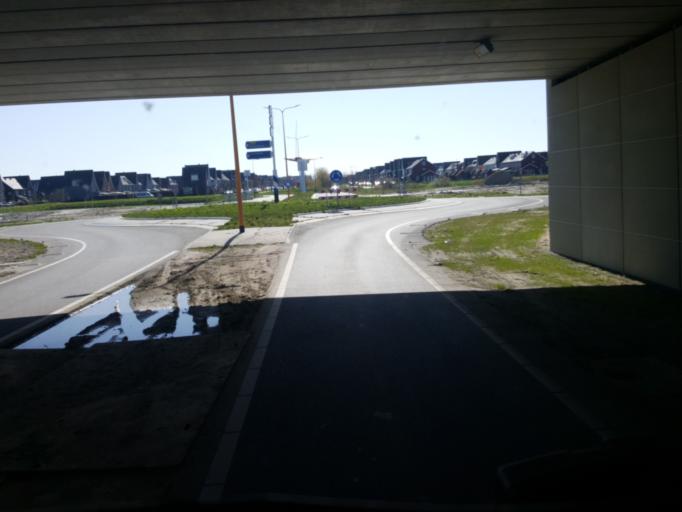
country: NL
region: North Holland
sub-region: Gemeente Hoorn
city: Hoorn
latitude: 52.6790
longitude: 5.0838
